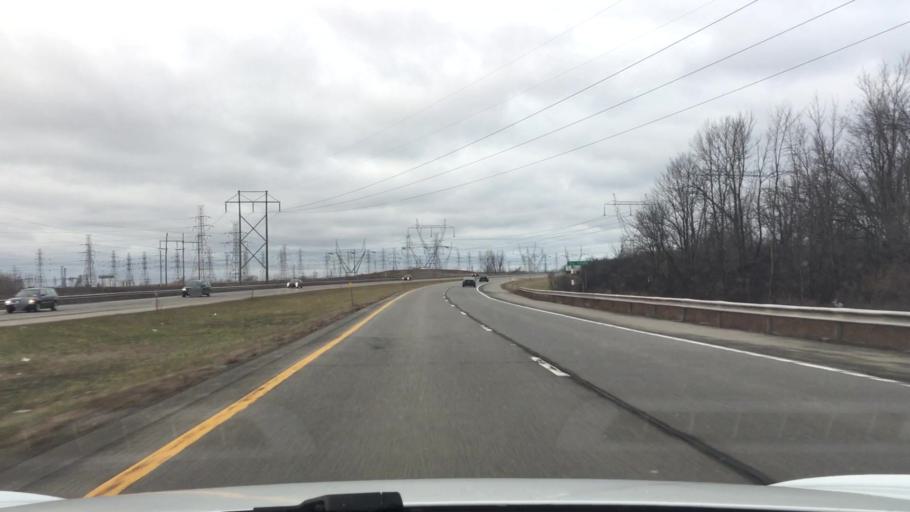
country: US
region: New York
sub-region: Niagara County
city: Niagara Falls
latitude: 43.1223
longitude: -79.0105
